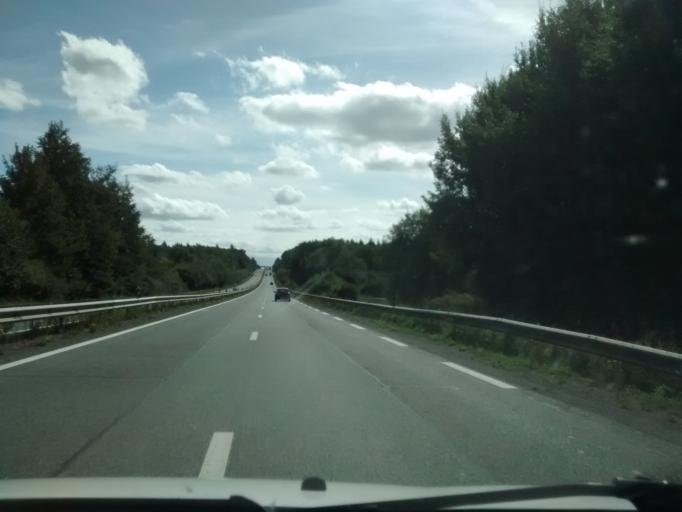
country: FR
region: Brittany
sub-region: Departement d'Ille-et-Vilaine
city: Miniac-Morvan
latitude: 48.5090
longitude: -1.9107
